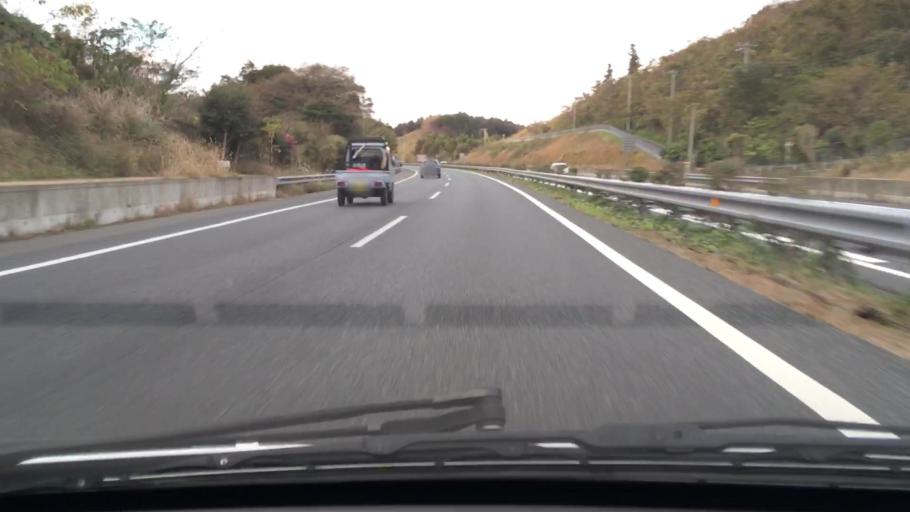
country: JP
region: Chiba
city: Kisarazu
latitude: 35.3266
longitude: 139.9463
